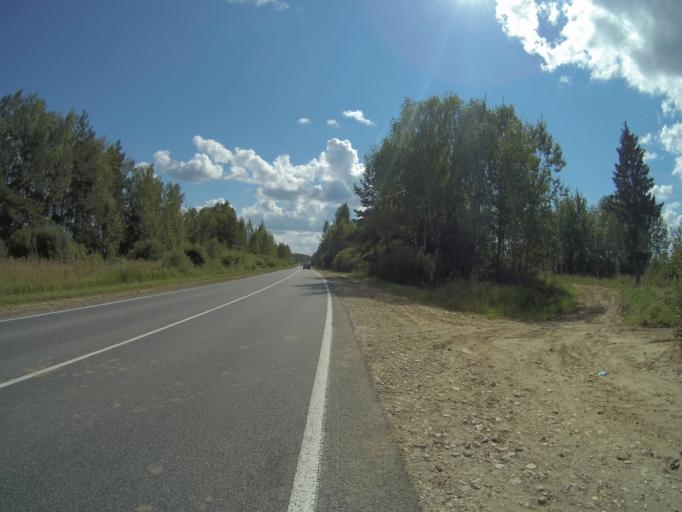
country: RU
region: Vladimir
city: Golovino
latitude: 55.9115
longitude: 40.6070
